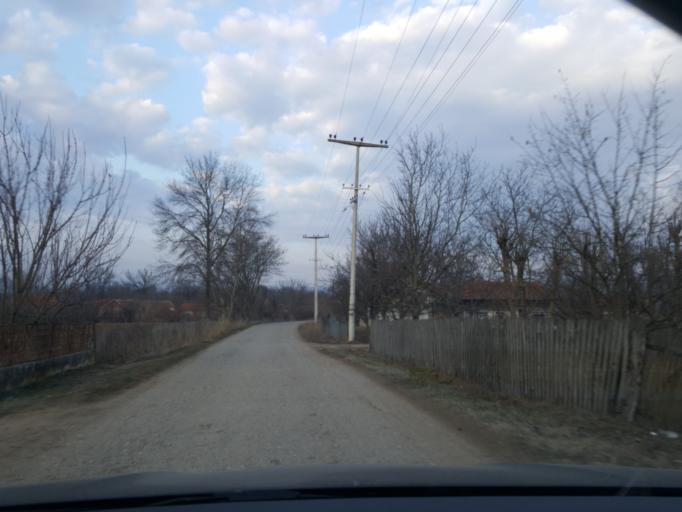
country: RS
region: Central Serbia
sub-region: Nisavski Okrug
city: Aleksinac
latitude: 43.5923
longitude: 21.6198
